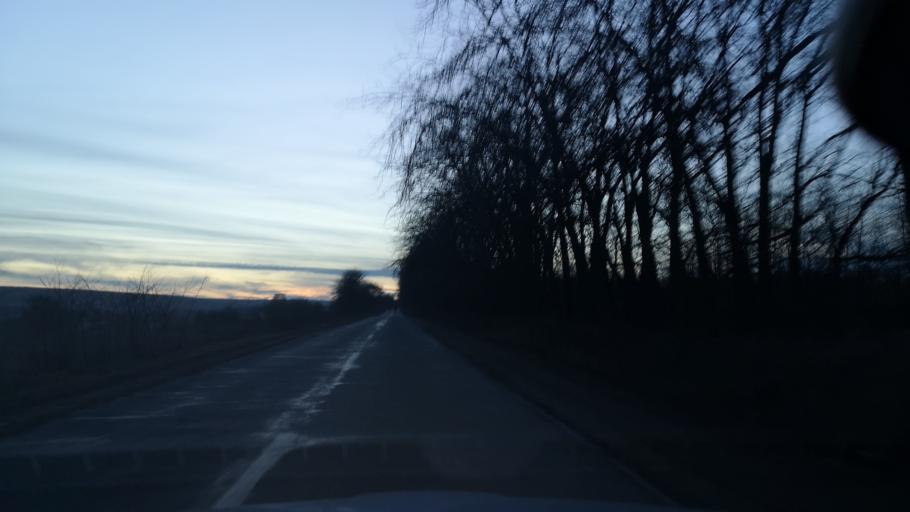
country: MD
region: Orhei
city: Orhei
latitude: 47.2960
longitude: 28.9022
